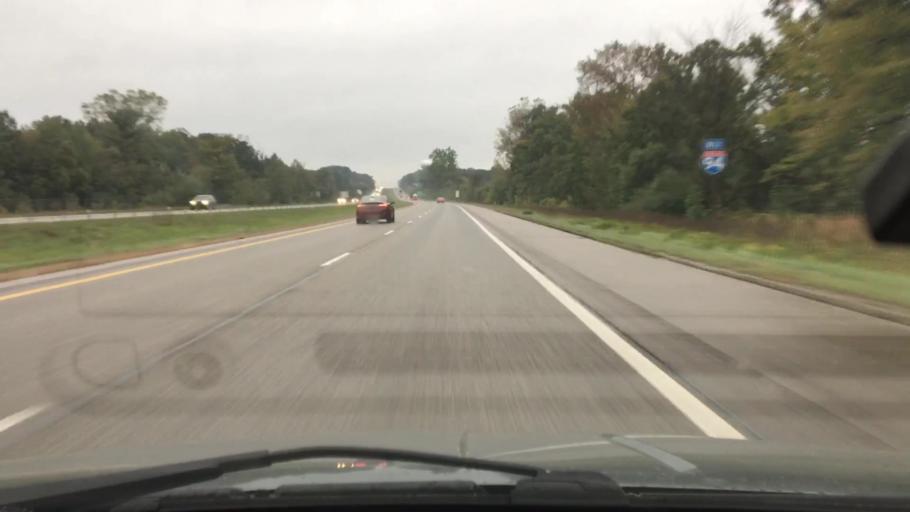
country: US
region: Michigan
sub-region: Washtenaw County
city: Chelsea
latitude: 42.2946
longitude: -84.0389
